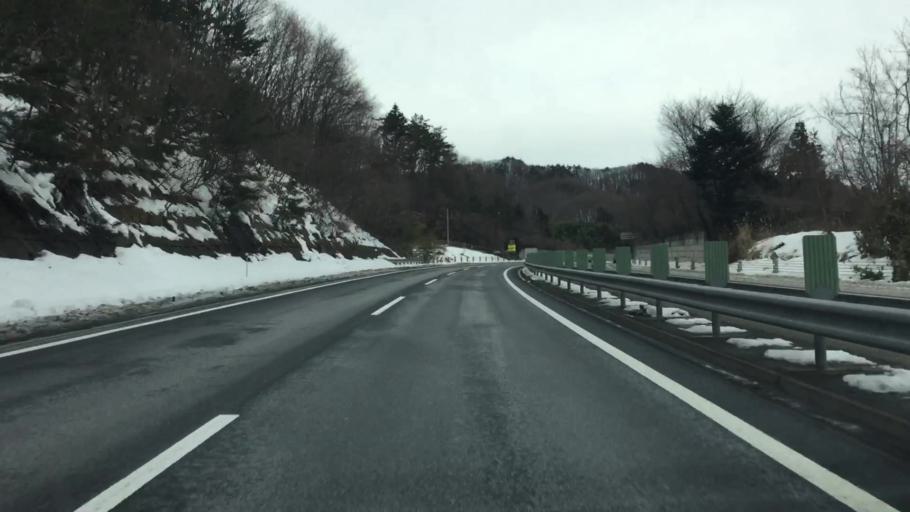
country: JP
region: Gunma
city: Numata
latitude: 36.7331
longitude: 138.9754
